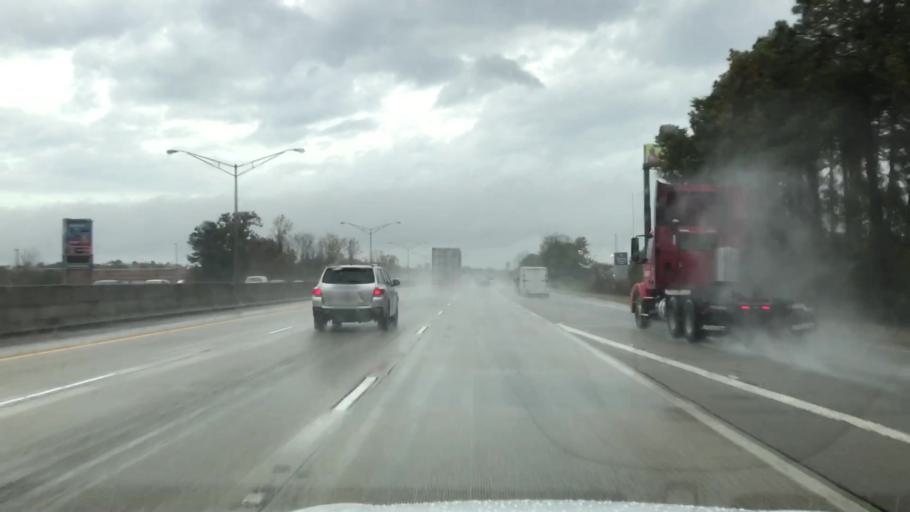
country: US
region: South Carolina
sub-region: Berkeley County
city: Hanahan
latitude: 32.8758
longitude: -80.0144
